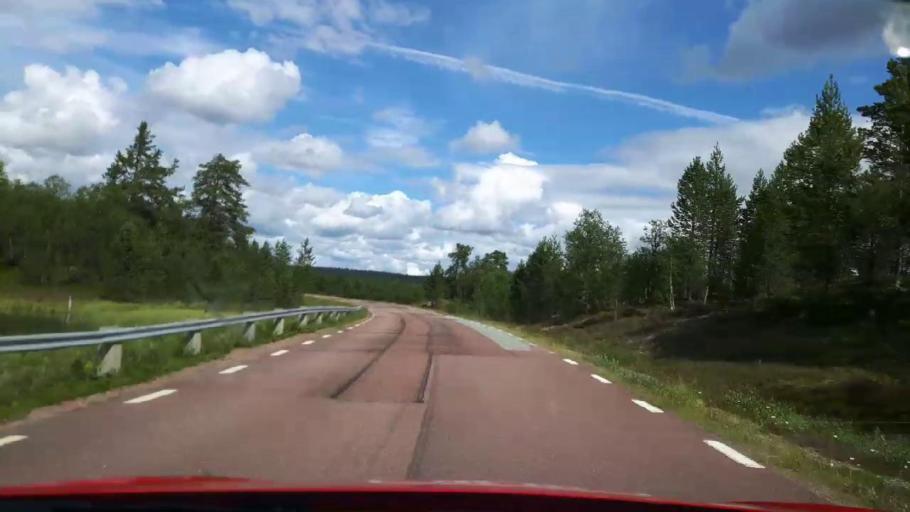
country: NO
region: Hedmark
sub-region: Trysil
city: Innbygda
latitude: 62.1009
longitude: 12.9813
